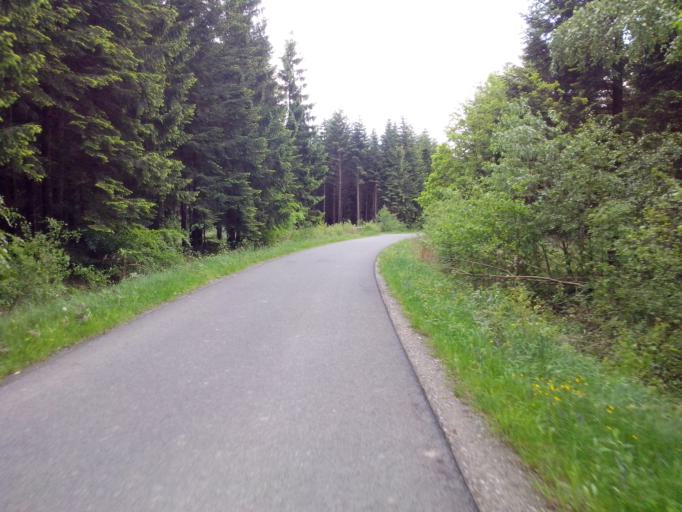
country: PL
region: Subcarpathian Voivodeship
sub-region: Powiat strzyzowski
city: Wysoka Strzyzowska
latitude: 49.8189
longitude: 21.7888
